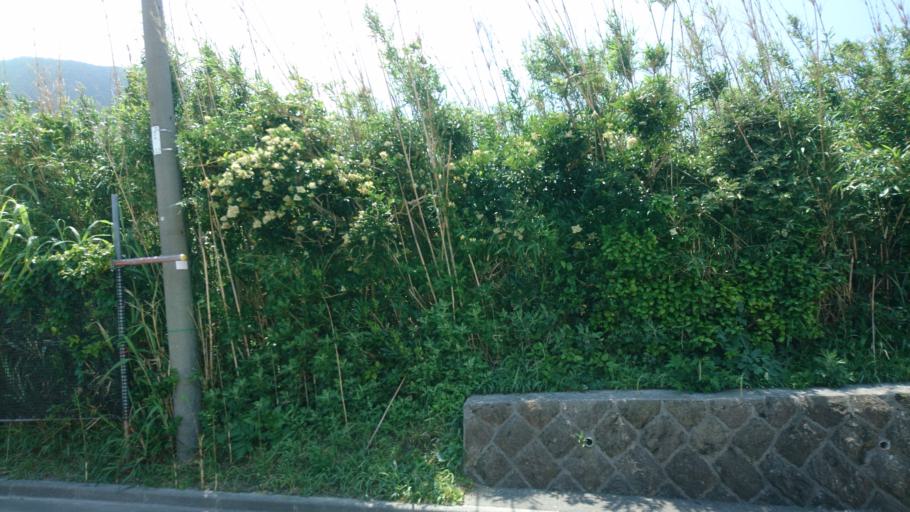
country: JP
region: Shizuoka
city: Shimoda
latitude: 34.4145
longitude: 139.2793
